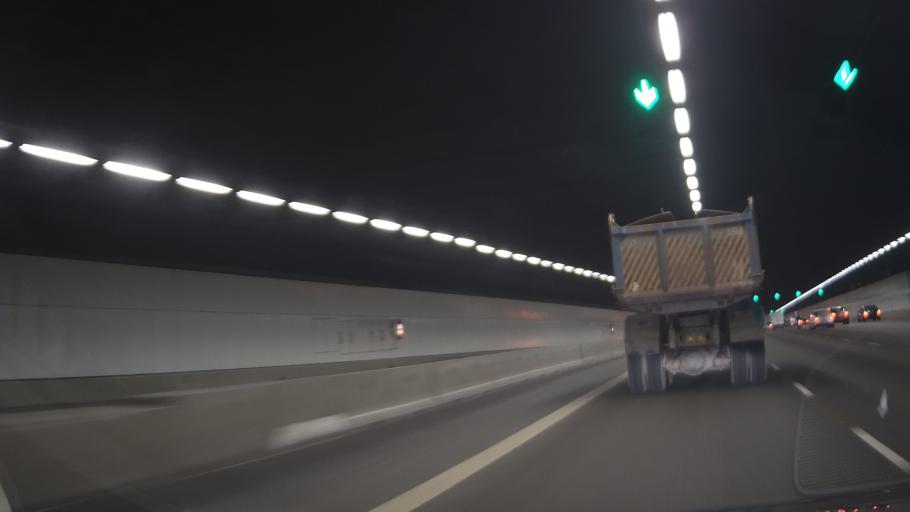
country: SG
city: Singapore
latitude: 1.2894
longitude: 103.8781
